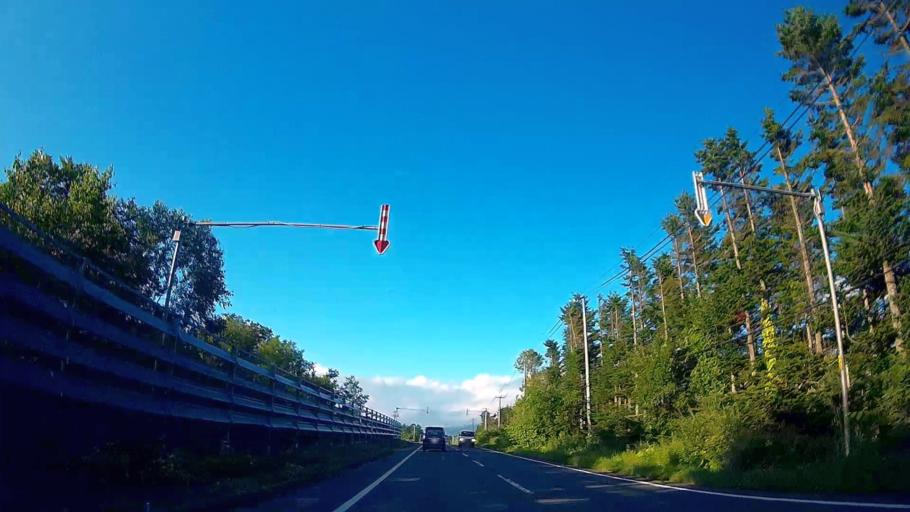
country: JP
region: Hokkaido
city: Date
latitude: 42.6199
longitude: 140.7929
